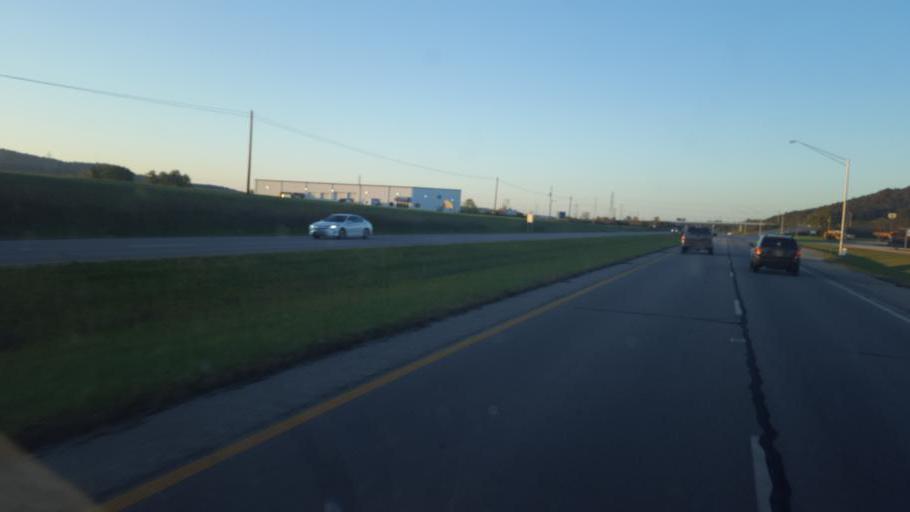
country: US
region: Ohio
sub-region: Pike County
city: Piketon
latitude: 39.0078
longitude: -83.0263
